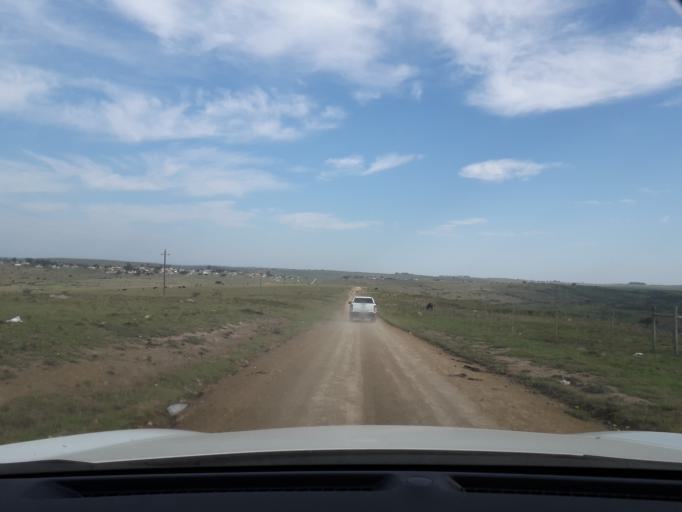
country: ZA
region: Eastern Cape
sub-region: Buffalo City Metropolitan Municipality
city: Bhisho
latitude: -32.9923
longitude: 27.3505
